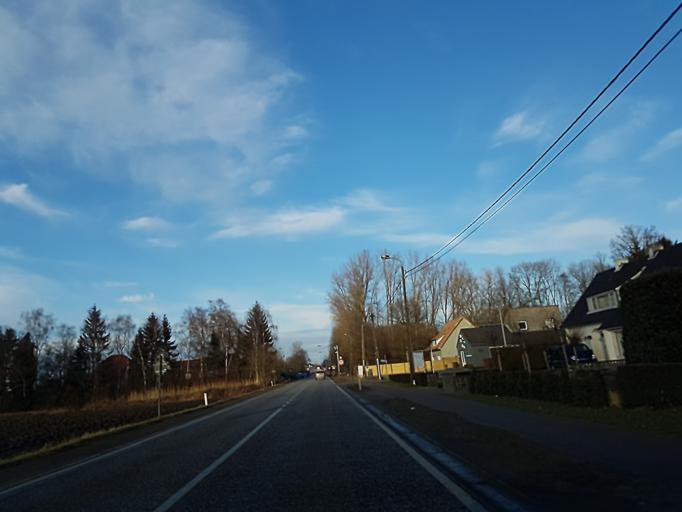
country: BE
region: Flanders
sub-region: Provincie Antwerpen
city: Ravels
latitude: 51.3533
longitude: 4.9860
